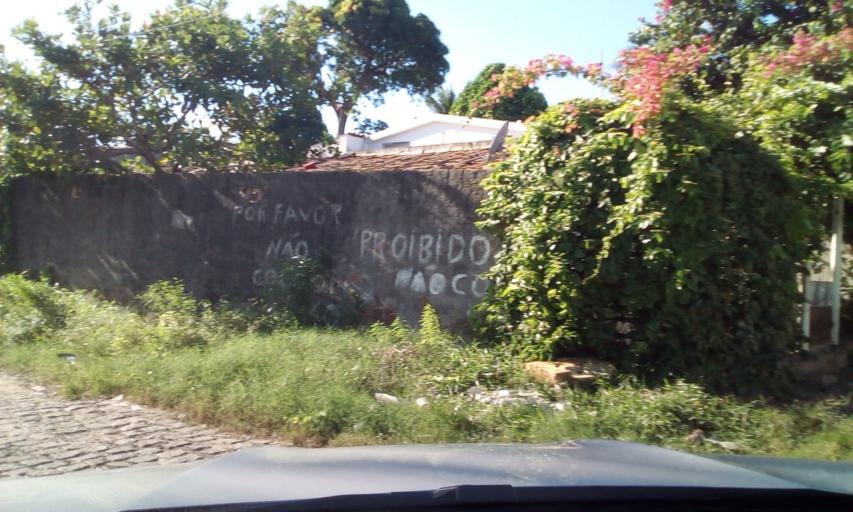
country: BR
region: Paraiba
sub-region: Joao Pessoa
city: Joao Pessoa
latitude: -7.1096
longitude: -34.8598
